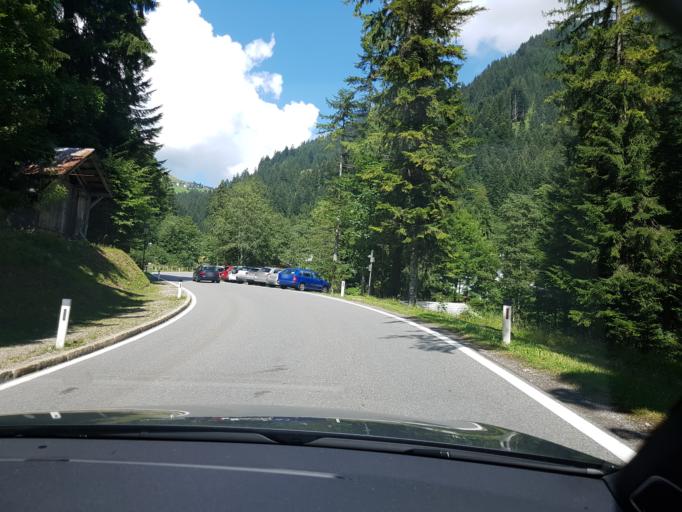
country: AT
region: Vorarlberg
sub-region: Politischer Bezirk Bregenz
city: Damuels
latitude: 47.2538
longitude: 9.9145
